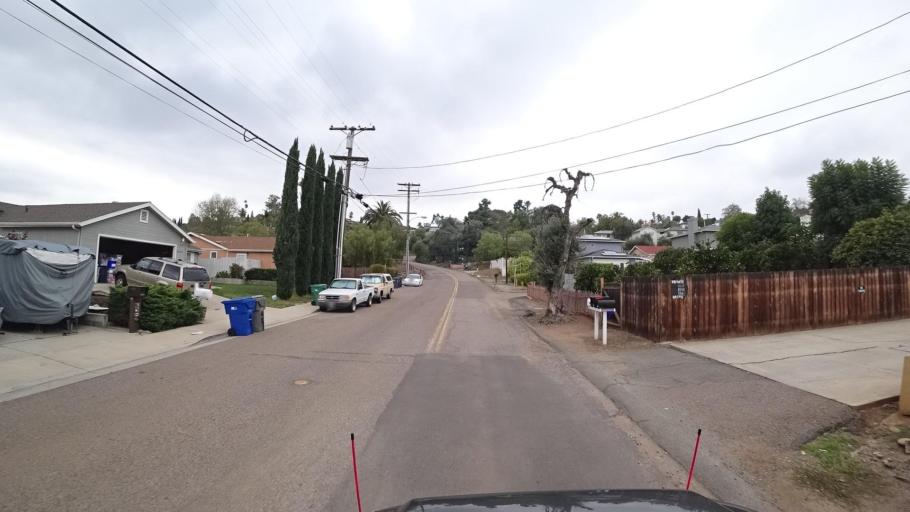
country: US
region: California
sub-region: San Diego County
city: Spring Valley
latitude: 32.7466
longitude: -117.0045
